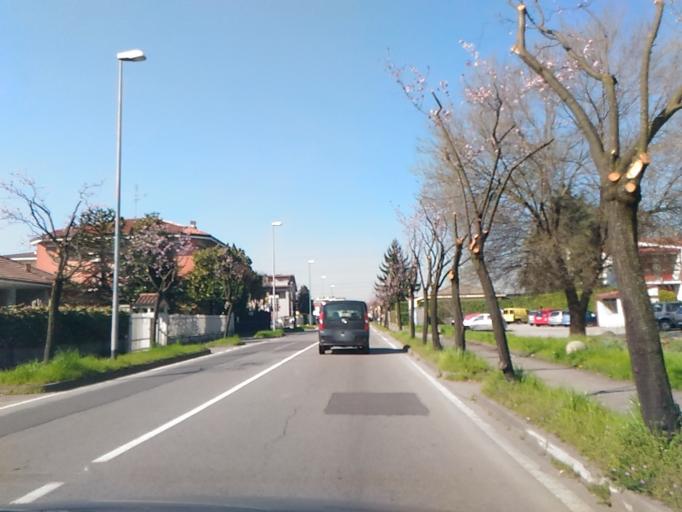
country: IT
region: Lombardy
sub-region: Provincia di Monza e Brianza
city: Brugherio
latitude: 45.5465
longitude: 9.3082
